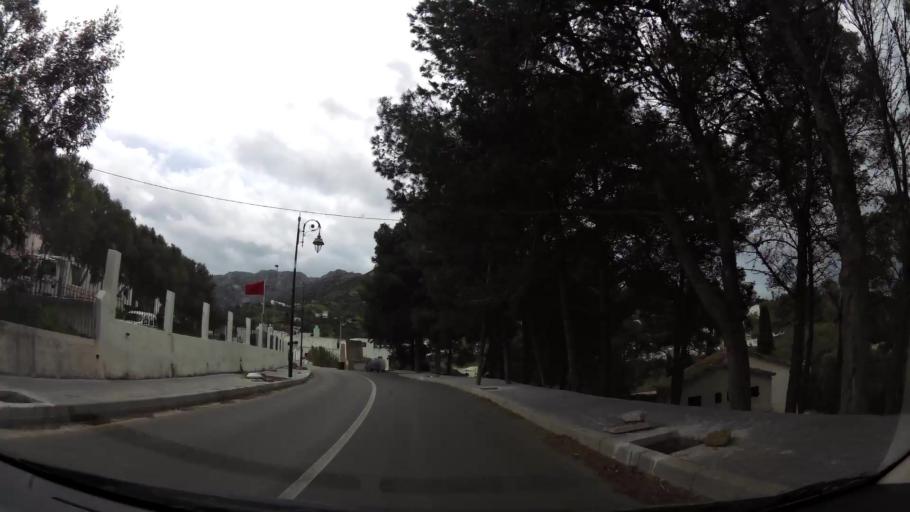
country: MA
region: Tanger-Tetouan
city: Tetouan
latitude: 35.5533
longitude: -5.3600
